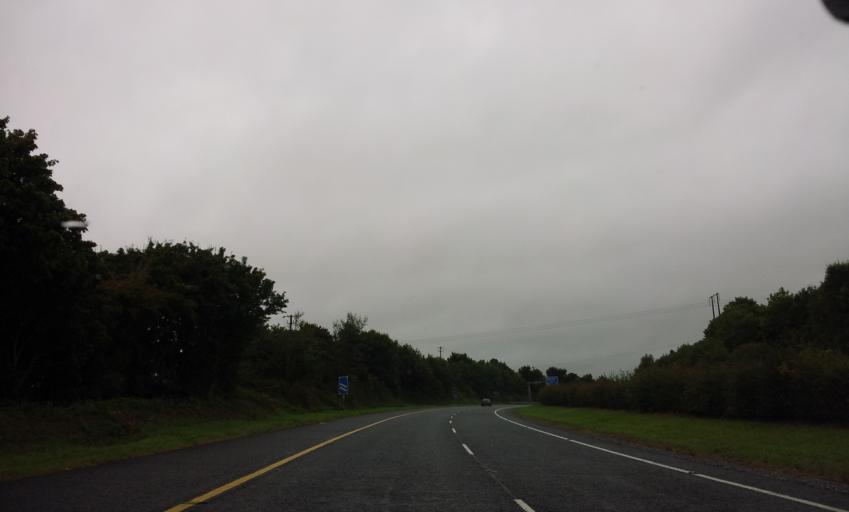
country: IE
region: Munster
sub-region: County Cork
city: Watergrasshill
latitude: 51.9442
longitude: -8.3930
